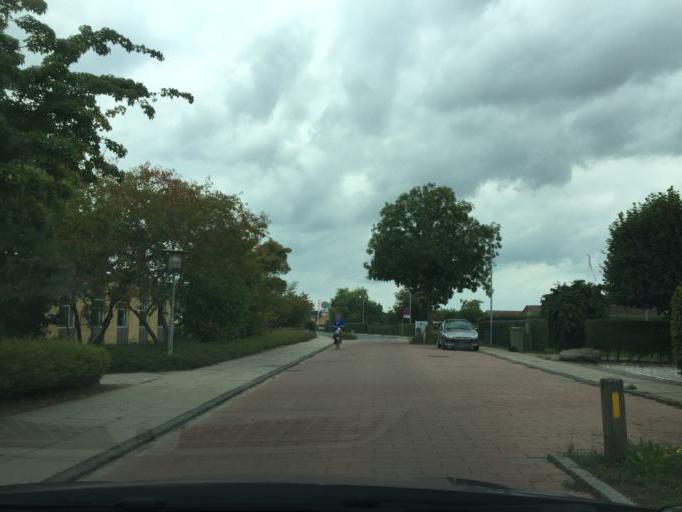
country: DK
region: South Denmark
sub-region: Odense Kommune
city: Stige
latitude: 55.4375
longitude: 10.4071
